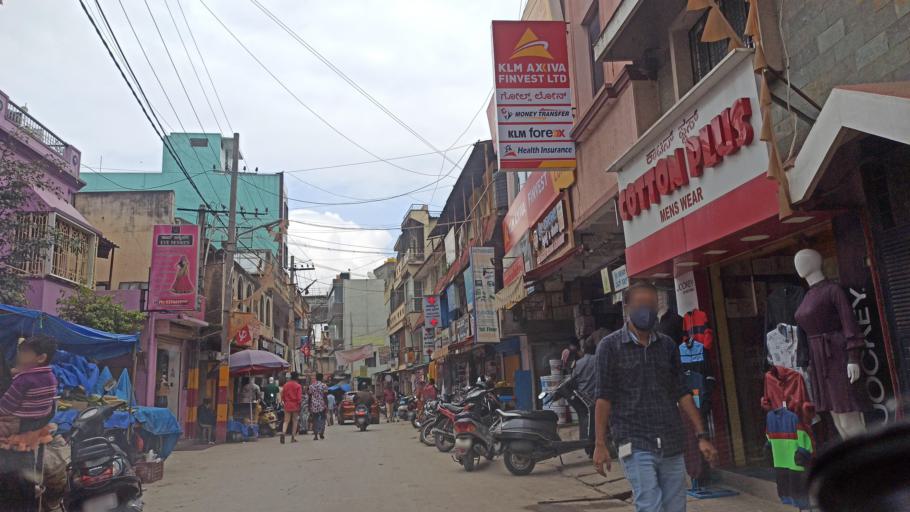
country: IN
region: Karnataka
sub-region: Bangalore Urban
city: Bangalore
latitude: 12.9966
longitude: 77.6721
